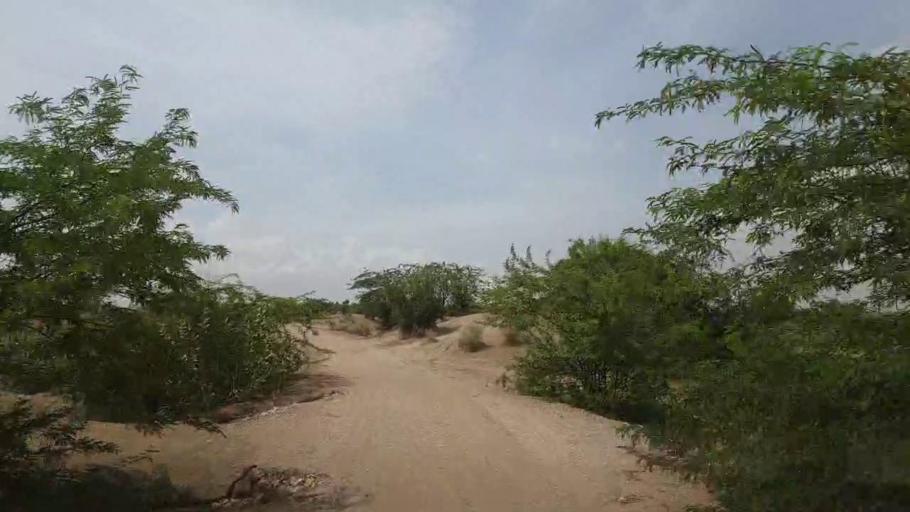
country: PK
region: Sindh
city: Kot Diji
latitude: 27.2525
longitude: 69.0757
